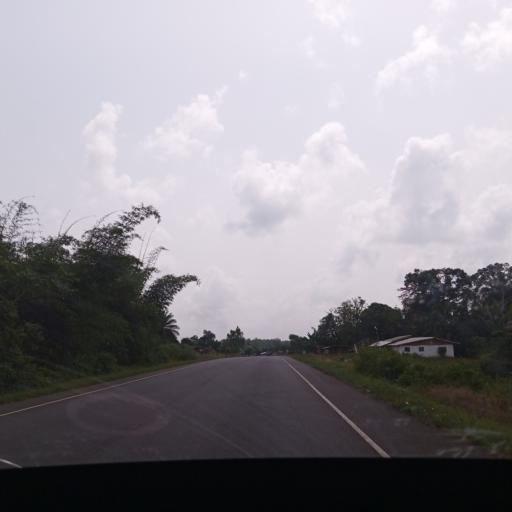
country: LR
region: Margibi
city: Kakata
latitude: 6.2374
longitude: -10.2838
